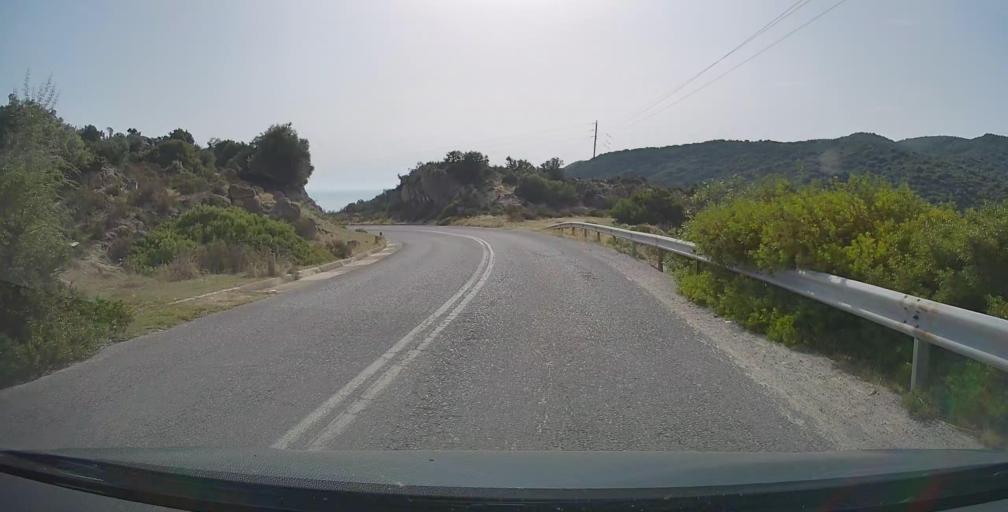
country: GR
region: Central Macedonia
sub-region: Nomos Chalkidikis
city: Sykia
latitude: 39.9883
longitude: 23.9724
